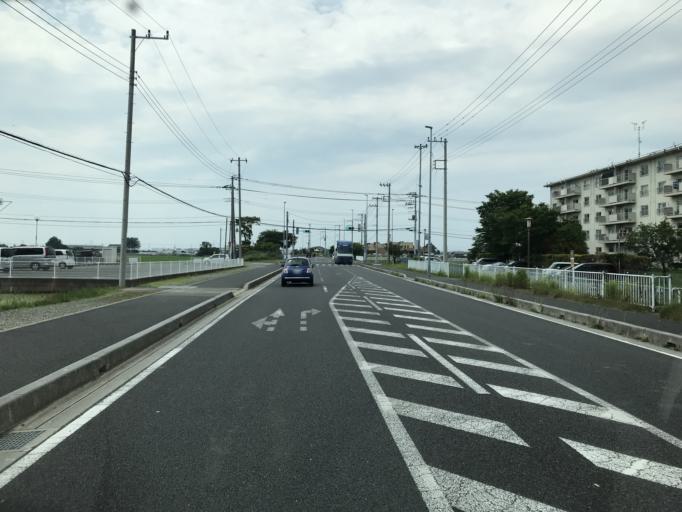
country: JP
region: Saitama
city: Kukichuo
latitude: 36.0854
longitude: 139.6581
